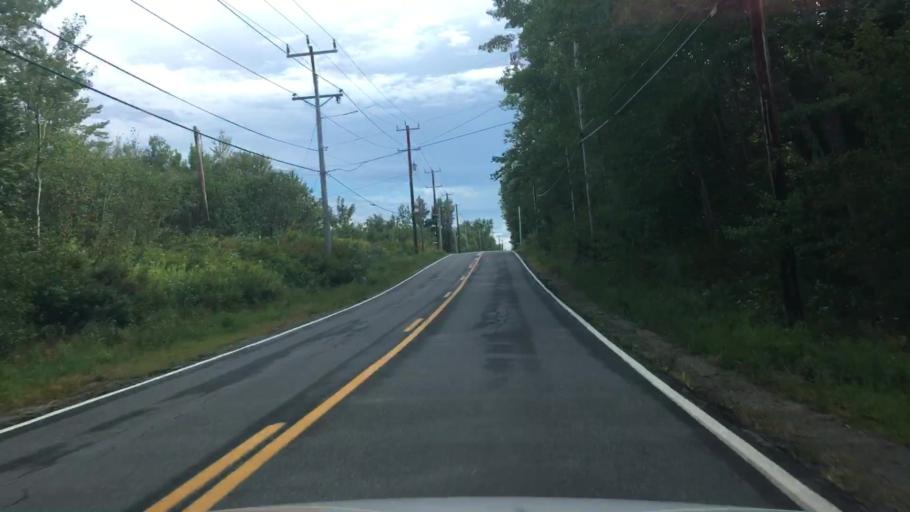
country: US
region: Maine
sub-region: Hancock County
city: Ellsworth
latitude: 44.4906
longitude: -68.4201
